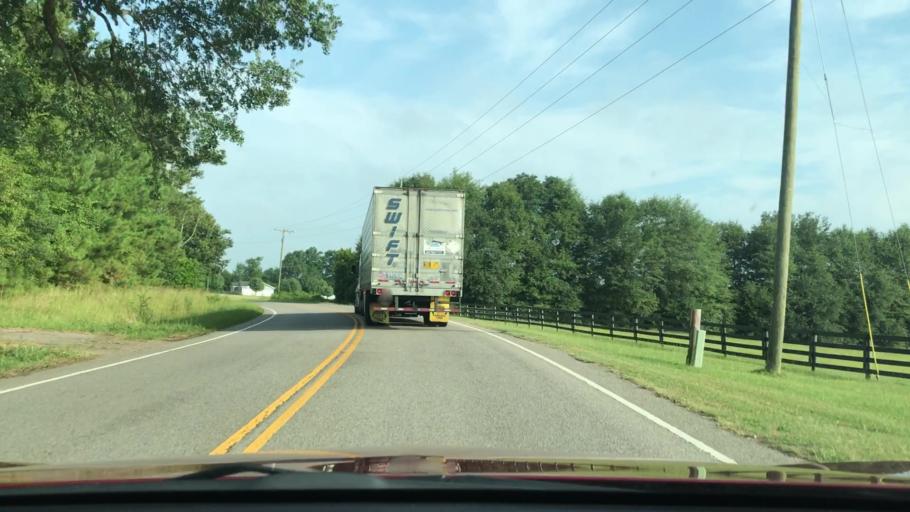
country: US
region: South Carolina
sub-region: Barnwell County
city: Blackville
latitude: 33.6062
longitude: -81.2674
